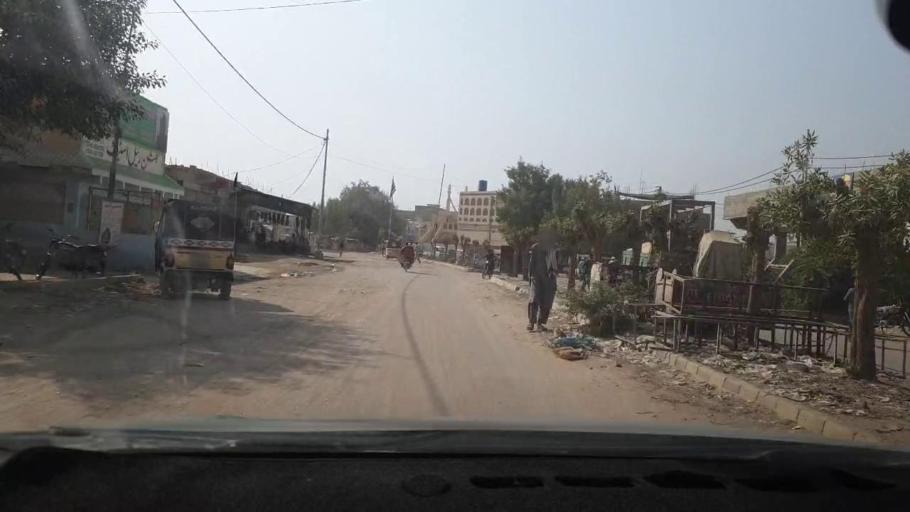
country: PK
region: Sindh
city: Malir Cantonment
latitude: 25.0101
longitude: 67.1596
